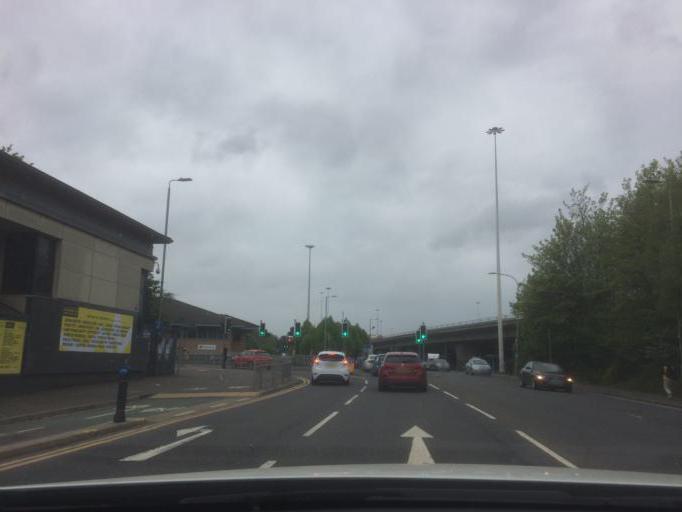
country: GB
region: Scotland
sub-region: Glasgow City
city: Glasgow
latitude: 55.8498
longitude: -4.2752
